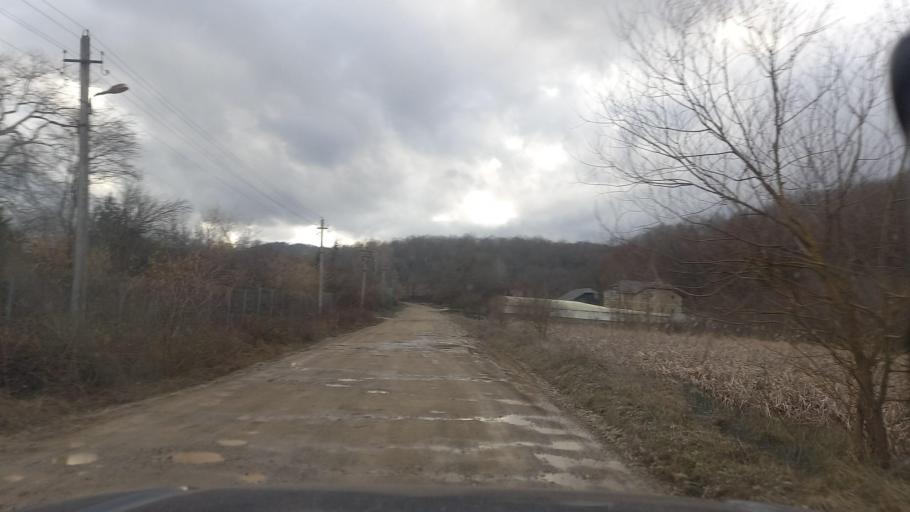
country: RU
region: Krasnodarskiy
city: Smolenskaya
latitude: 44.5647
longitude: 38.8020
